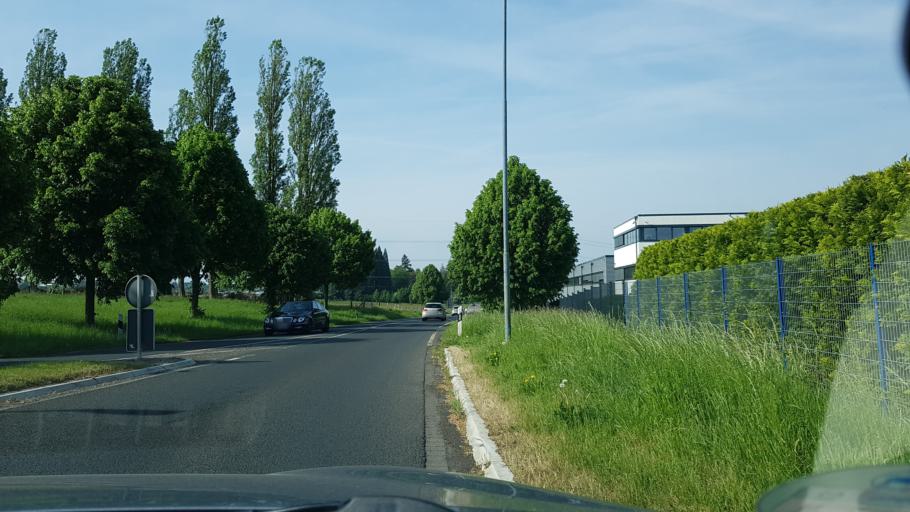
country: DE
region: Rheinland-Pfalz
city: Neuhausel
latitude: 50.3807
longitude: 7.7045
